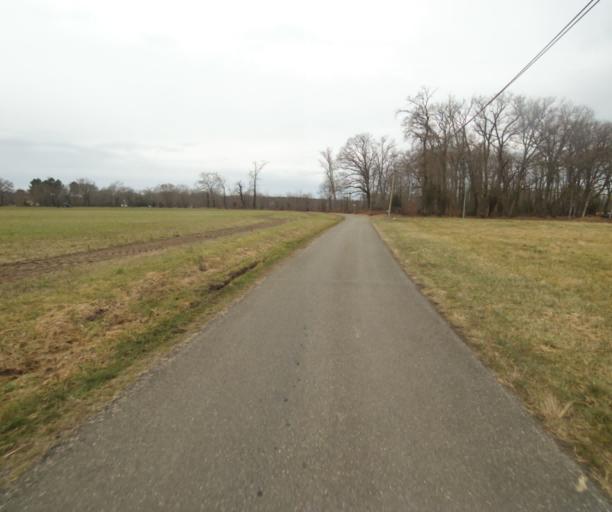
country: FR
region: Aquitaine
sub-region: Departement des Landes
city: Gabarret
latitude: 44.0128
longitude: -0.0286
